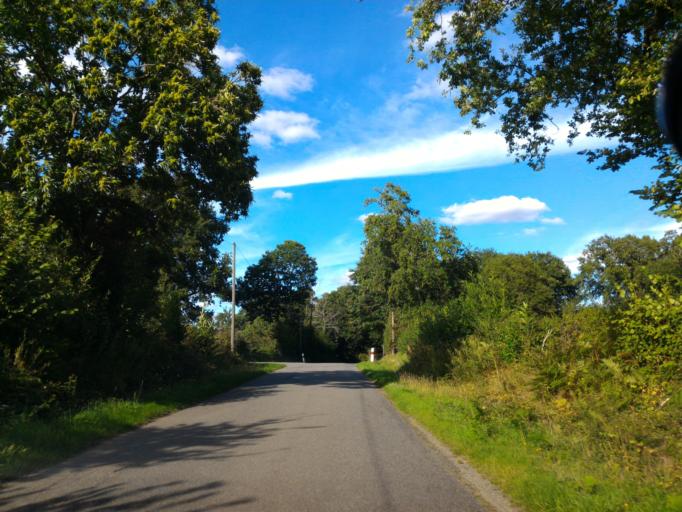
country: FR
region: Poitou-Charentes
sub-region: Departement de la Charente
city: Brigueuil
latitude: 45.9987
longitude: 0.8435
